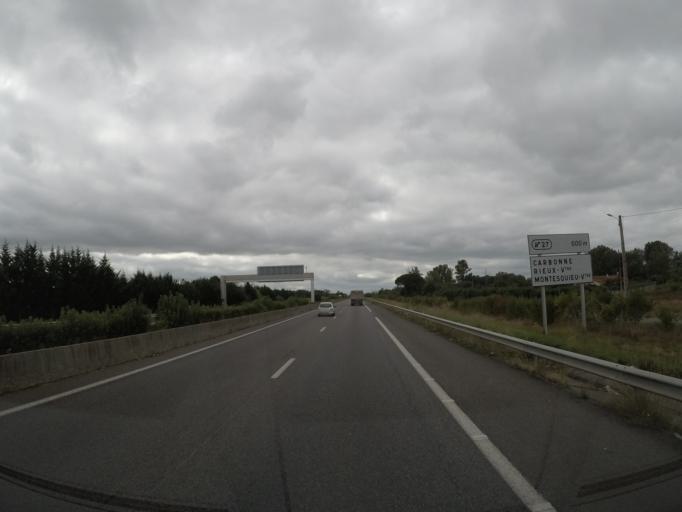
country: FR
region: Midi-Pyrenees
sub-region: Departement de la Haute-Garonne
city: Marquefave
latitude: 43.3260
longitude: 1.2279
